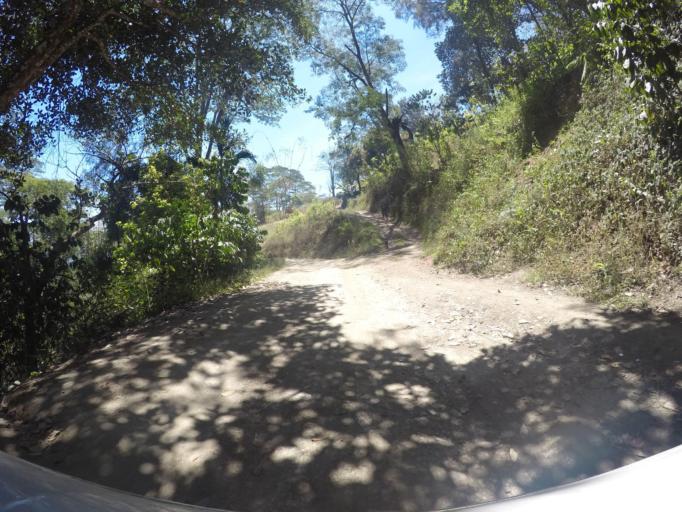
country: TL
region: Ermera
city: Gleno
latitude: -8.7371
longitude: 125.4089
